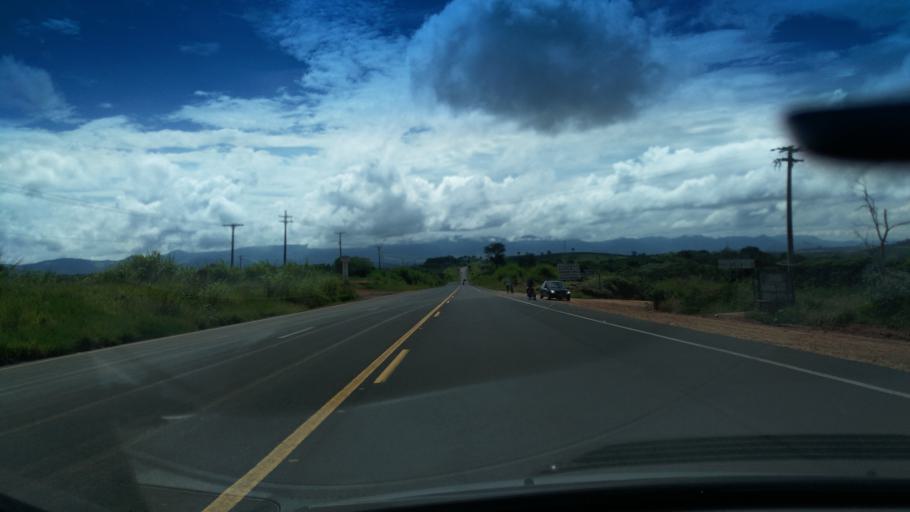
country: BR
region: Sao Paulo
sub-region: Santo Antonio Do Jardim
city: Espirito Santo do Pinhal
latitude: -22.1510
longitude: -46.7210
